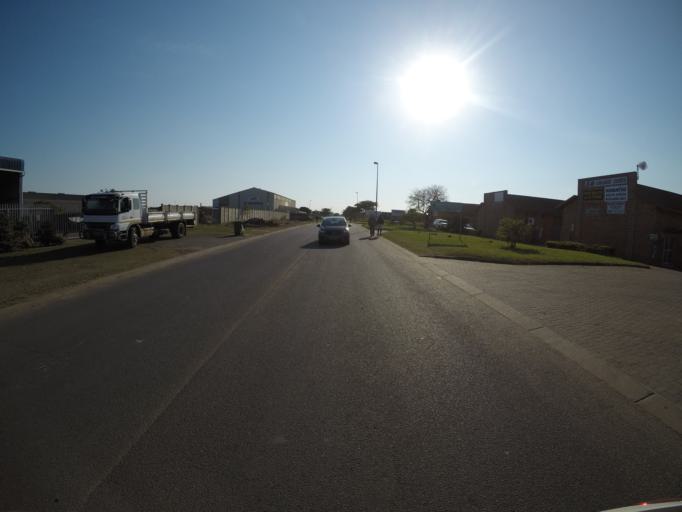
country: ZA
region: KwaZulu-Natal
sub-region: uThungulu District Municipality
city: Richards Bay
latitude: -28.7452
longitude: 32.0355
